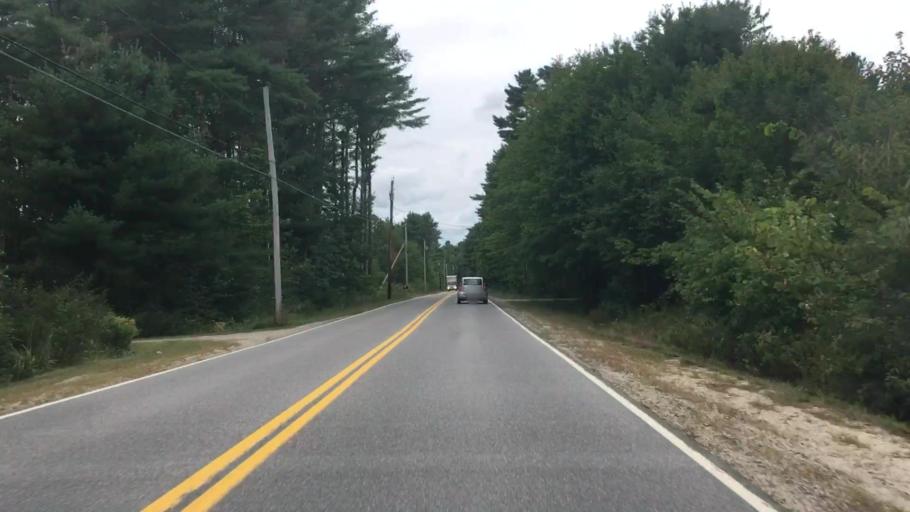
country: US
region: Maine
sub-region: Cumberland County
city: Cumberland Center
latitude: 43.8690
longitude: -70.2291
